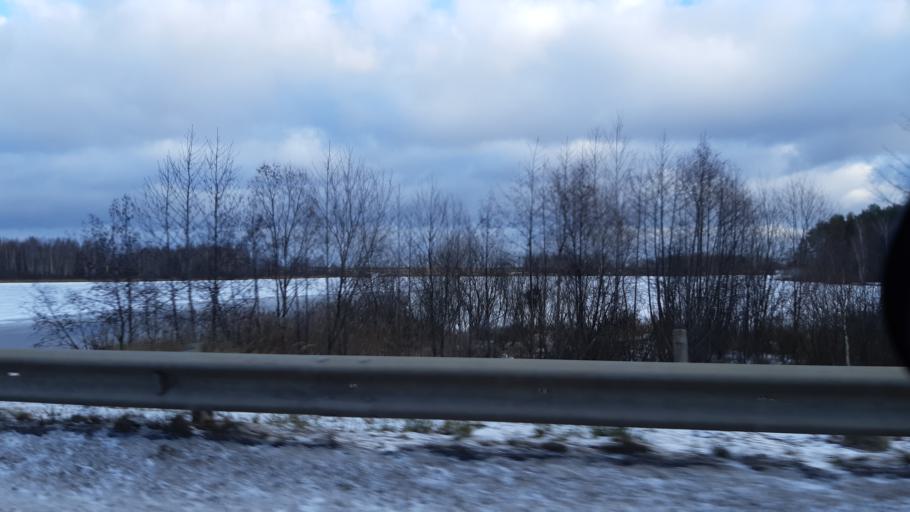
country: RU
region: Moskovskaya
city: Noginsk-9
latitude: 55.9825
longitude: 38.5441
